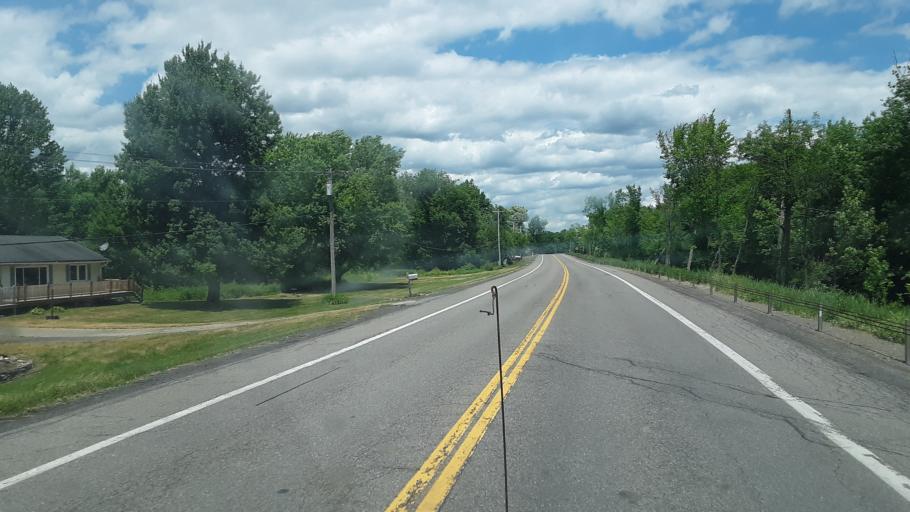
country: US
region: New York
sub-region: Madison County
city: Oneida
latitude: 43.1736
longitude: -75.6477
